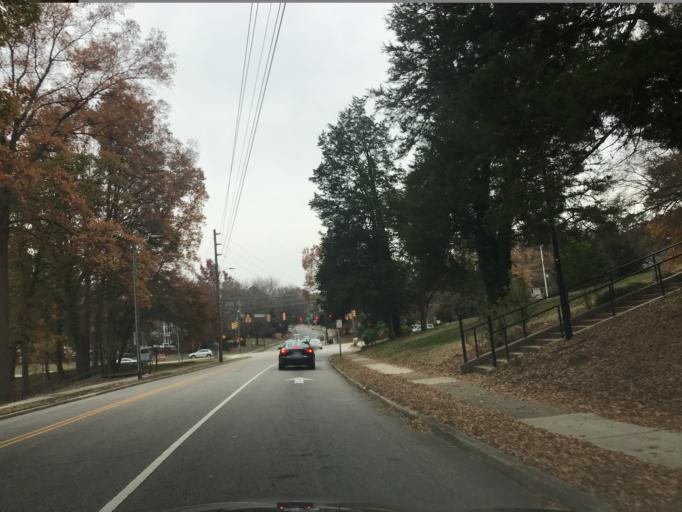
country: US
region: North Carolina
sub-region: Wake County
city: West Raleigh
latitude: 35.7968
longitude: -78.6528
